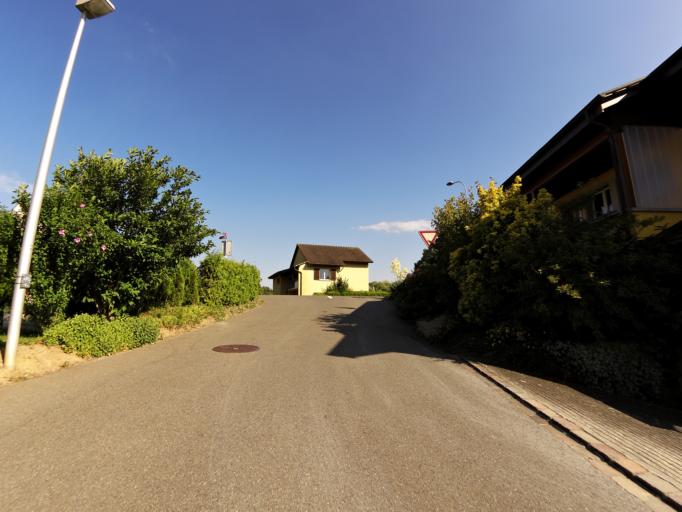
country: CH
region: Aargau
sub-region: Bezirk Lenzburg
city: Niederlenz
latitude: 47.4145
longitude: 8.1787
